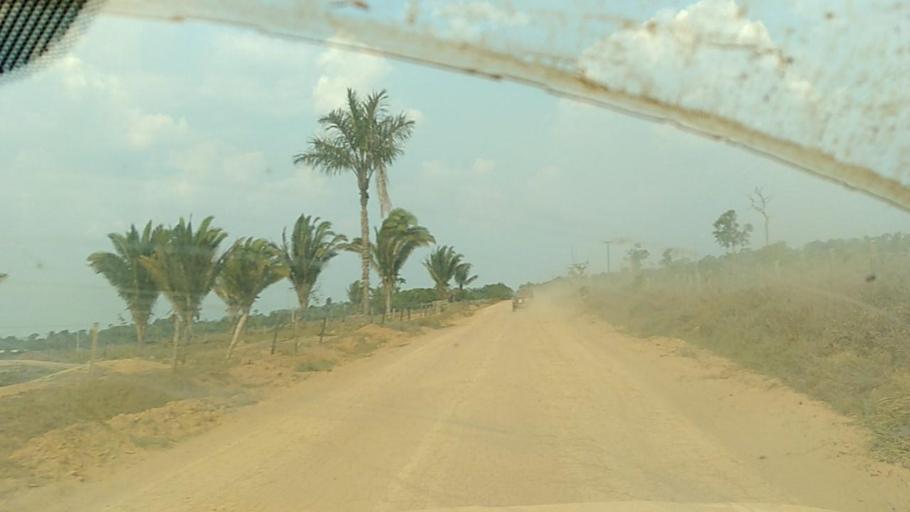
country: BR
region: Rondonia
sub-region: Porto Velho
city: Porto Velho
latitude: -8.6833
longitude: -63.2360
